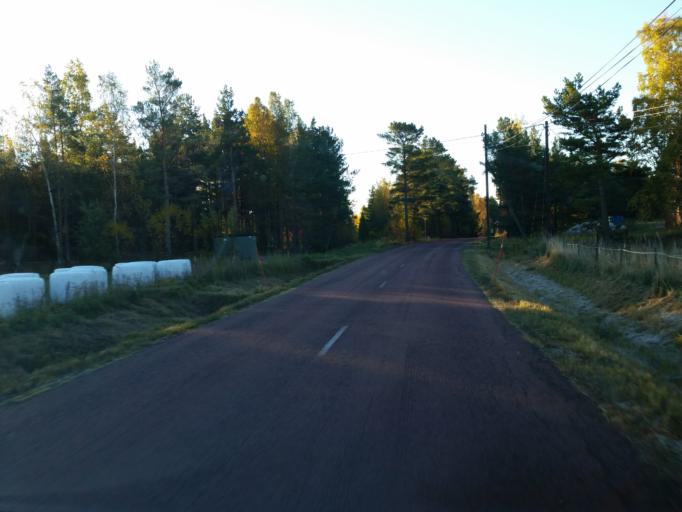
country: AX
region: Alands skaergard
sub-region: Vardoe
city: Vardoe
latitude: 60.2948
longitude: 20.3862
